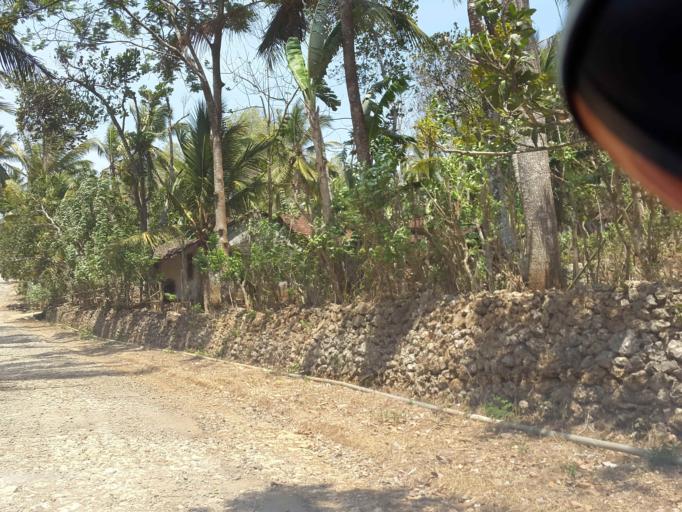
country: ID
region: East Java
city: Krajan
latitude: -8.1778
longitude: 110.9093
